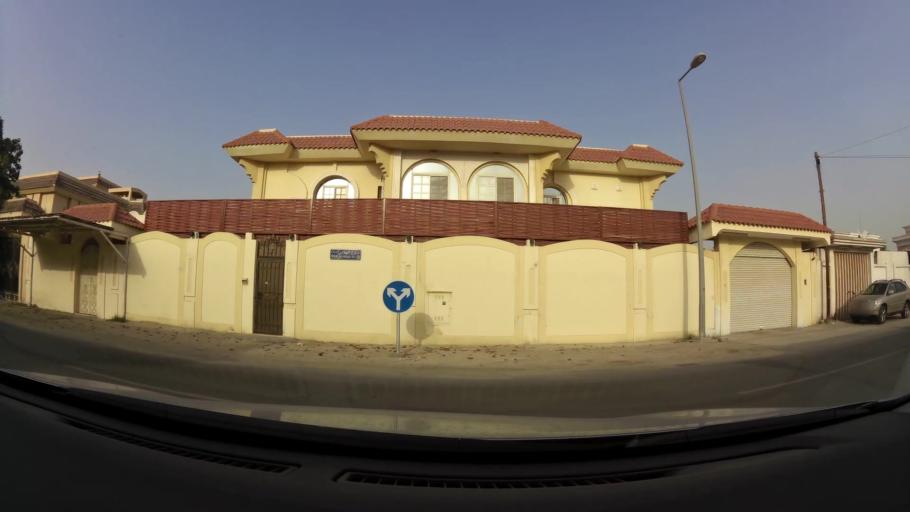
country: QA
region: Baladiyat ar Rayyan
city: Ar Rayyan
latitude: 25.2527
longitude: 51.4465
